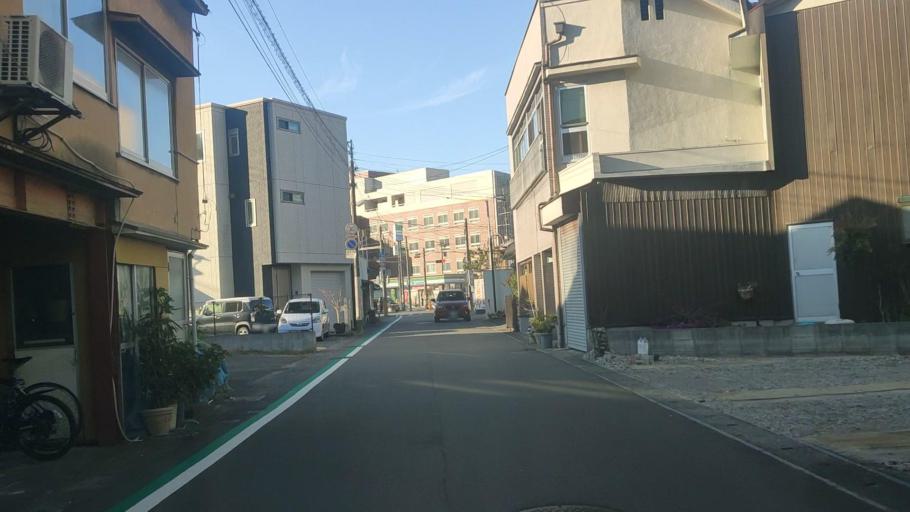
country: JP
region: Oita
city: Beppu
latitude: 33.2725
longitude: 131.5039
